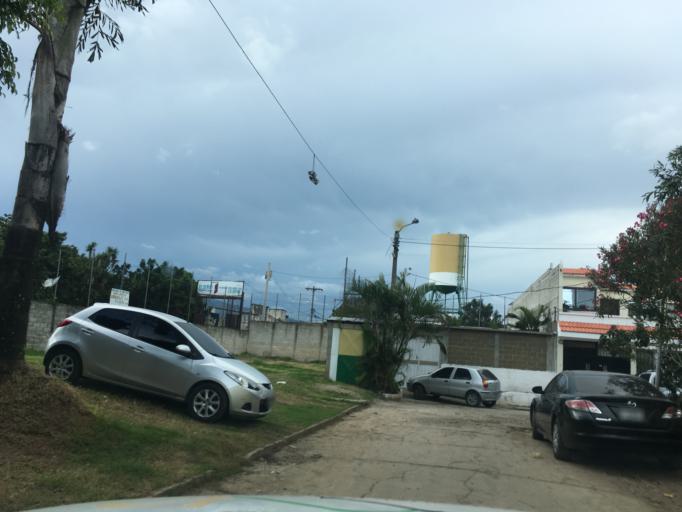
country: GT
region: Guatemala
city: Petapa
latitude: 14.5020
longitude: -90.5654
